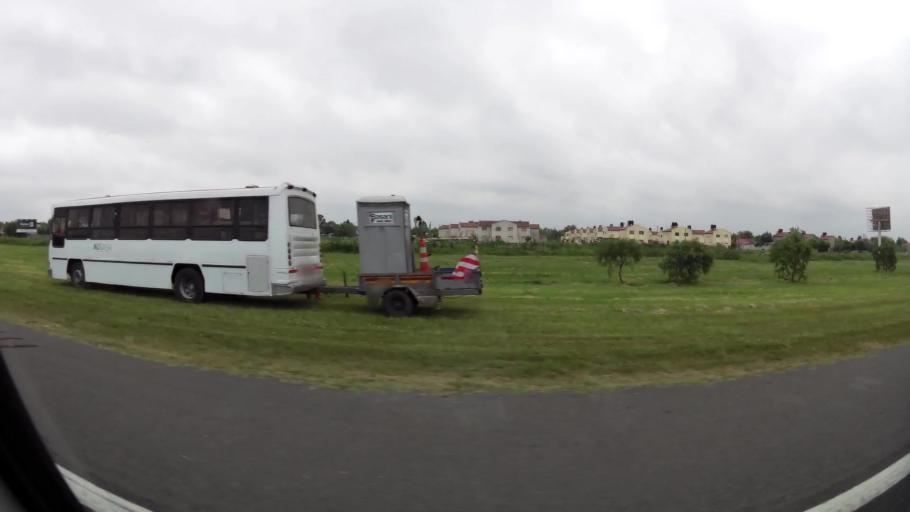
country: AR
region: Buenos Aires
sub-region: Partido de La Plata
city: La Plata
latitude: -34.8766
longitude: -57.9694
